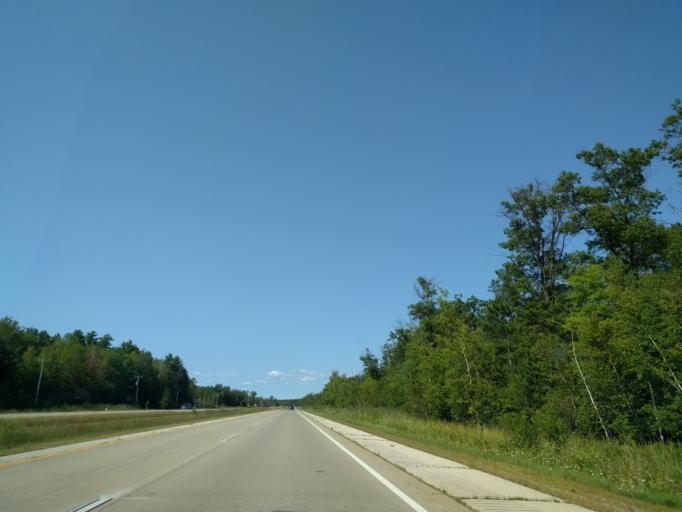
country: US
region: Wisconsin
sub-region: Oconto County
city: Oconto
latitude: 44.8569
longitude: -87.8990
